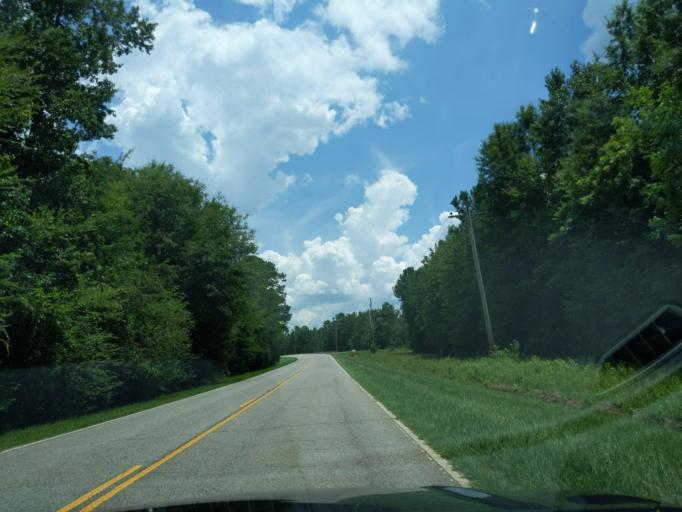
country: US
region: South Carolina
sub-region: Edgefield County
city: Edgefield
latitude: 33.8756
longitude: -82.0102
